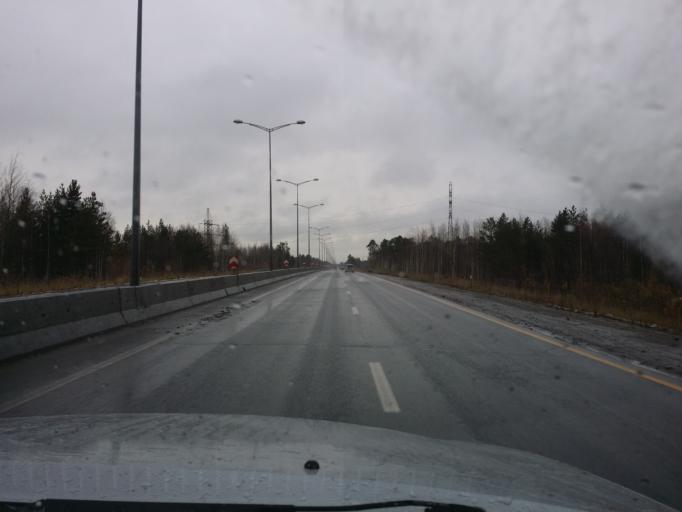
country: RU
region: Khanty-Mansiyskiy Avtonomnyy Okrug
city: Nizhnevartovsk
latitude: 60.9976
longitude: 76.4253
